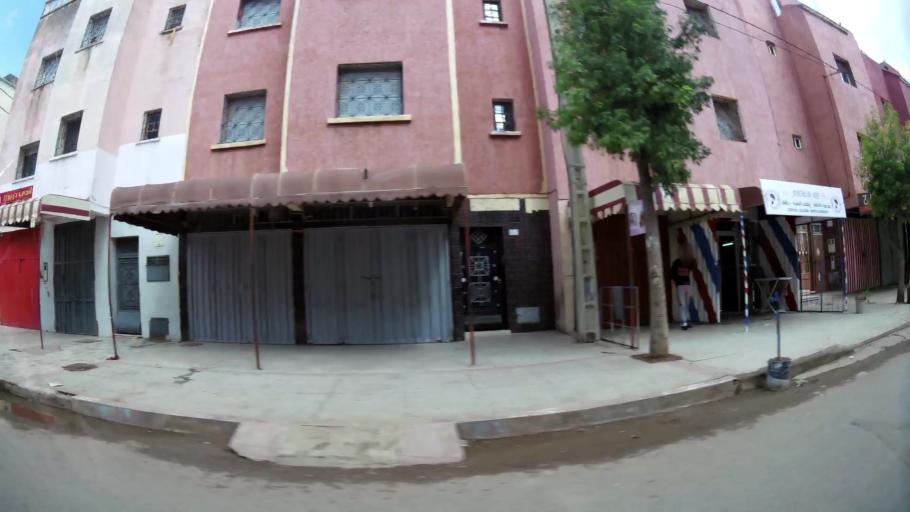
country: MA
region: Grand Casablanca
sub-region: Mediouna
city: Mediouna
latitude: 33.3684
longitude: -7.5292
